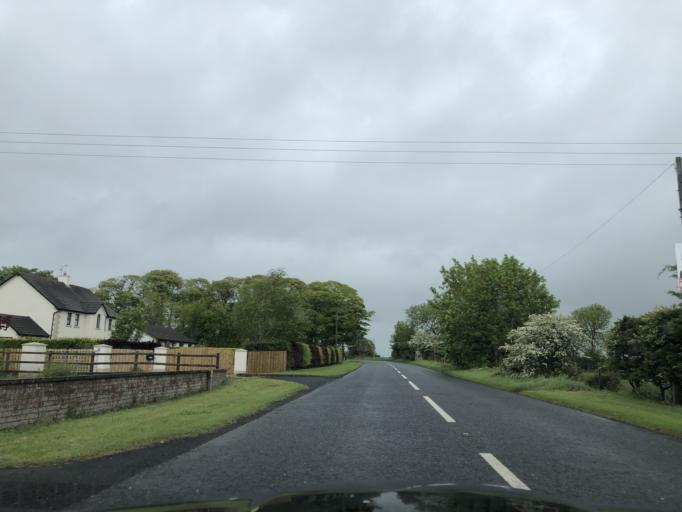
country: GB
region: Northern Ireland
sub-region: Moyle District
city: Ballycastle
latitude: 55.1780
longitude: -6.3292
